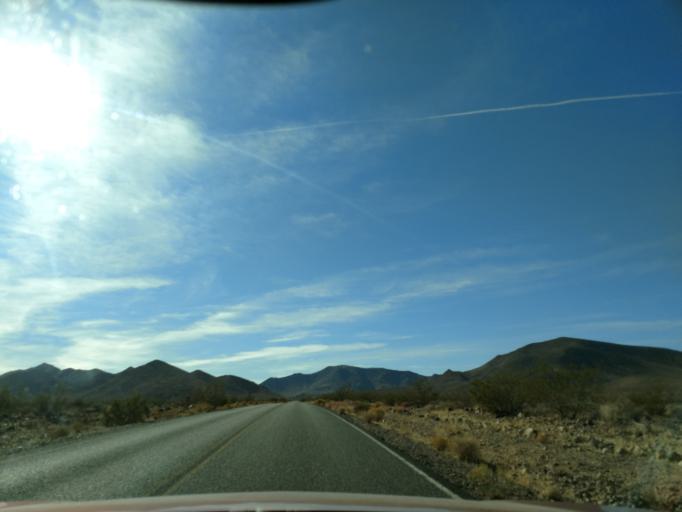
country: US
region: Nevada
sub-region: Nye County
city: Beatty
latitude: 36.8192
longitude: -116.8971
